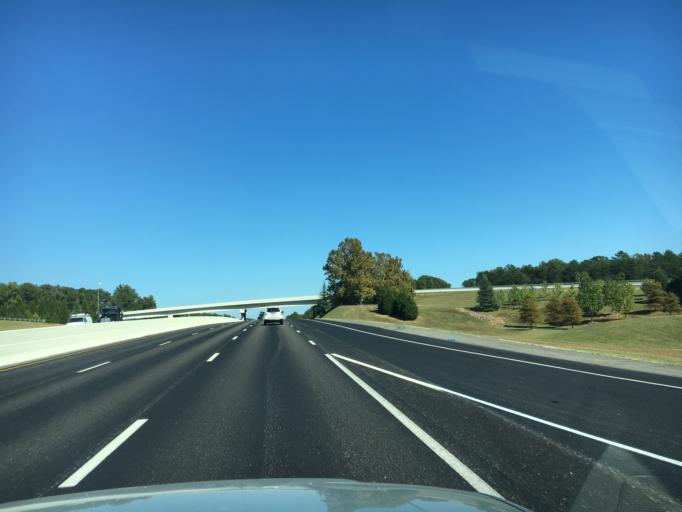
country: US
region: South Carolina
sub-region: Greenville County
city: Greer
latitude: 34.8758
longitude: -82.2158
